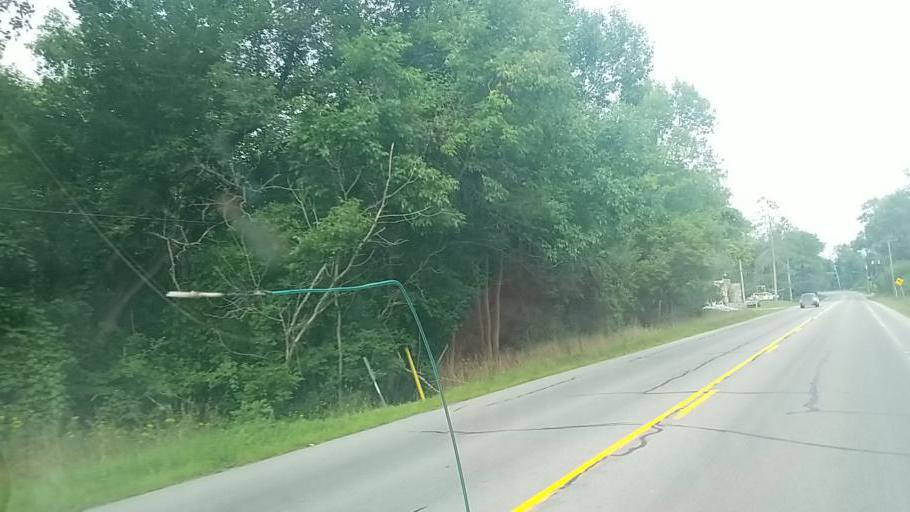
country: US
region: New York
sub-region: Montgomery County
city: Fort Plain
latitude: 42.9243
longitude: -74.6019
